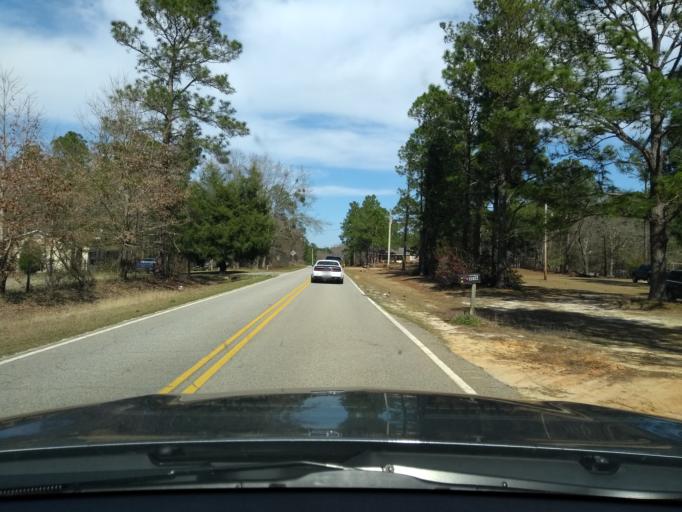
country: US
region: Georgia
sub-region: Bulloch County
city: Brooklet
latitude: 32.4723
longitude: -81.6368
